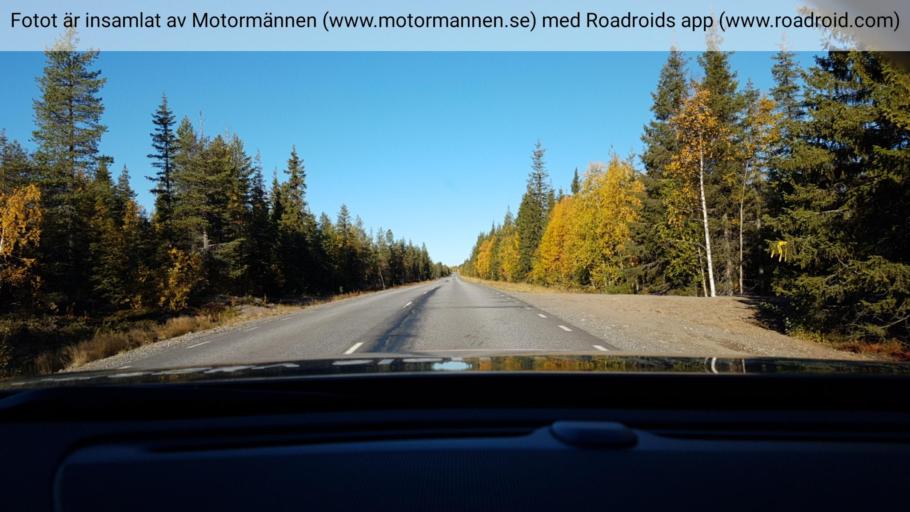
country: SE
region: Vaesterbotten
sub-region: Skelleftea Kommun
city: Storvik
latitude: 65.3556
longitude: 20.4688
